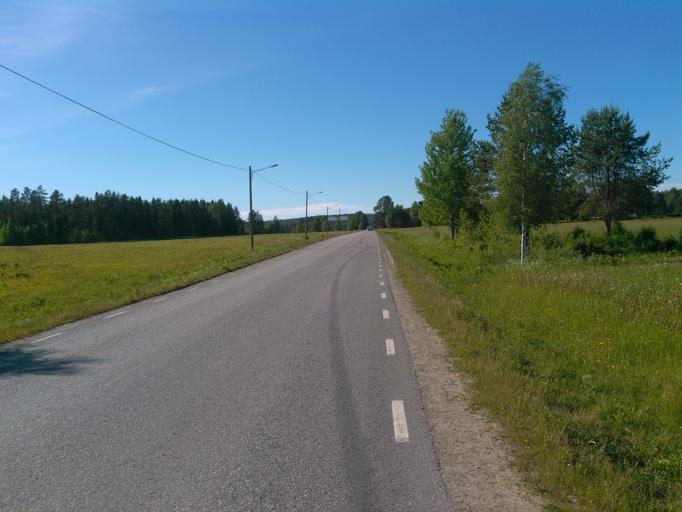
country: SE
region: Vaesterbotten
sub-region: Umea Kommun
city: Roback
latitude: 63.8268
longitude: 20.1199
